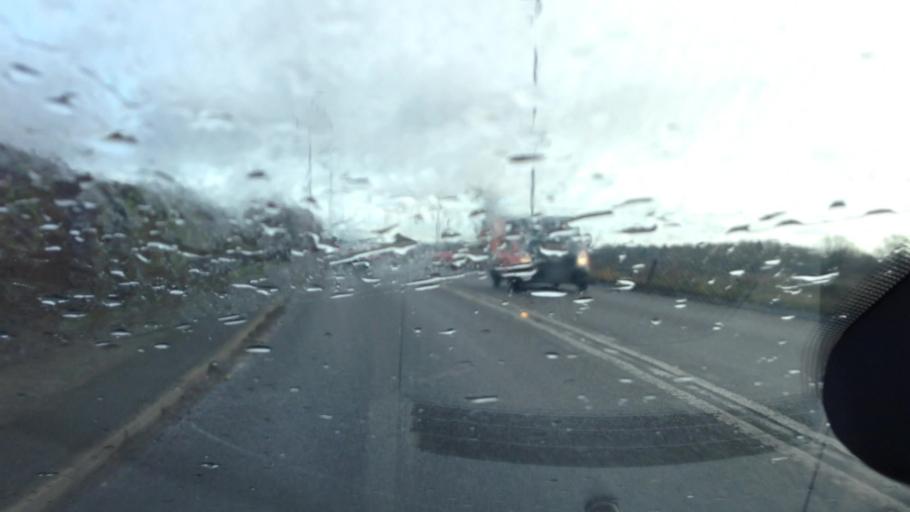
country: GB
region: England
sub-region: City and Borough of Leeds
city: Garforth
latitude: 53.7814
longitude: -1.3706
